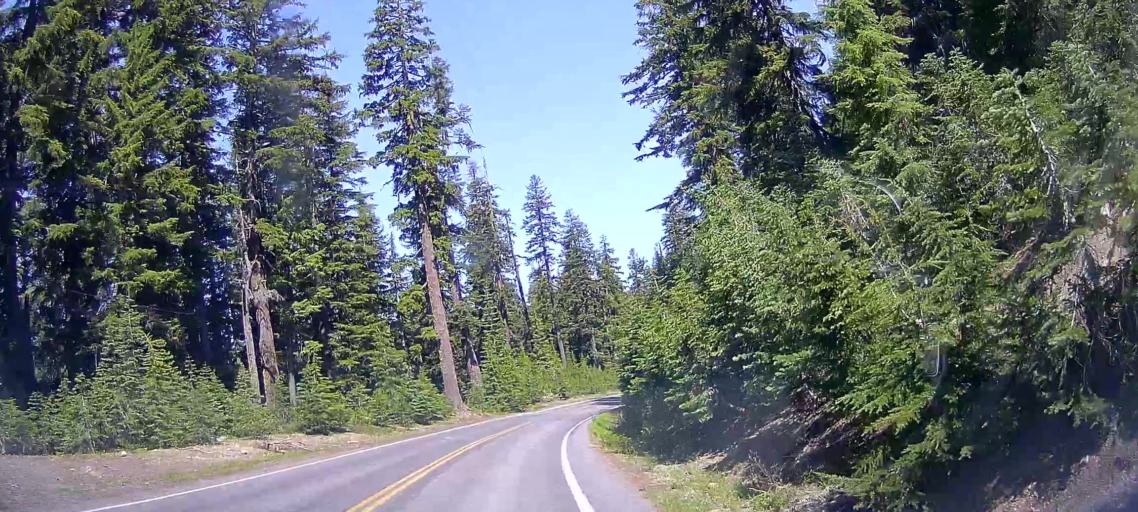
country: US
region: Oregon
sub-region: Jackson County
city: Shady Cove
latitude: 42.8818
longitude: -122.1283
